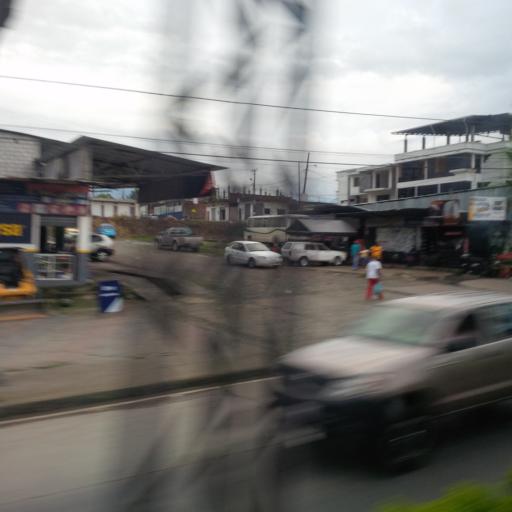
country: EC
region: Chimborazo
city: Alausi
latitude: -2.2062
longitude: -79.1334
